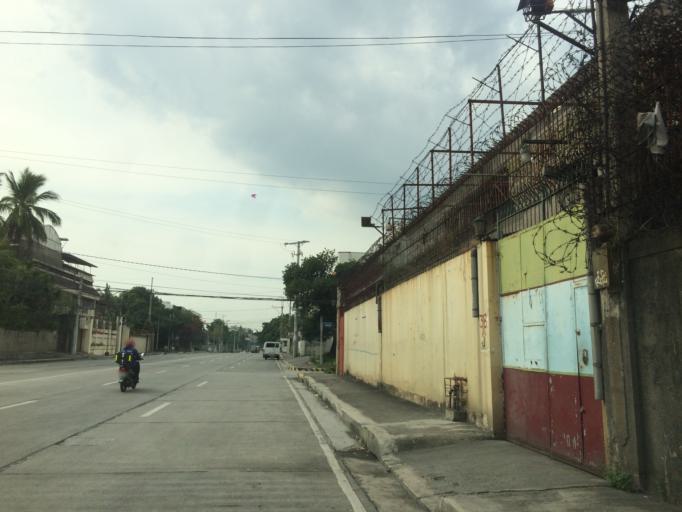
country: PH
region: Calabarzon
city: Del Monte
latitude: 14.6298
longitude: 121.0084
